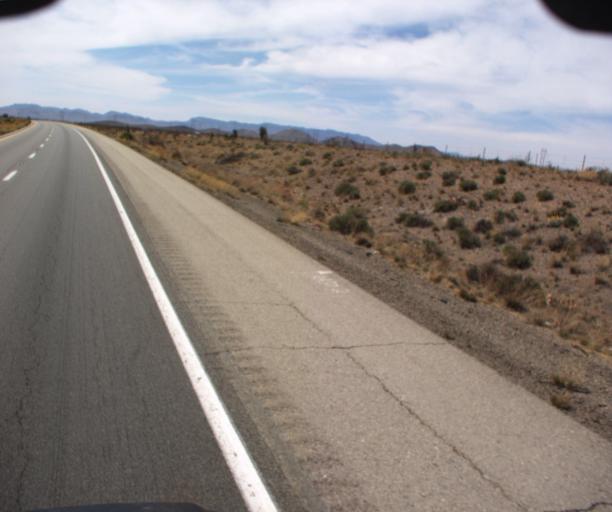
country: US
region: Arizona
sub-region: Cochise County
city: Willcox
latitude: 32.3492
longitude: -109.7410
